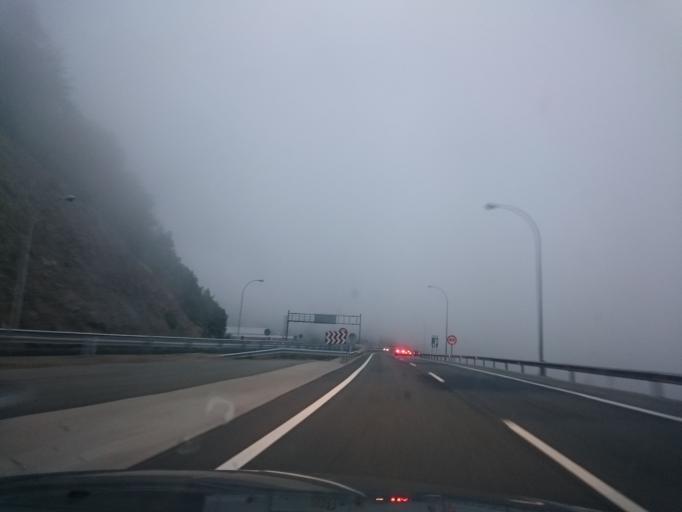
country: ES
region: Castille and Leon
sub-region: Provincia de Leon
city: Sena de Luna
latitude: 42.9796
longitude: -5.8309
